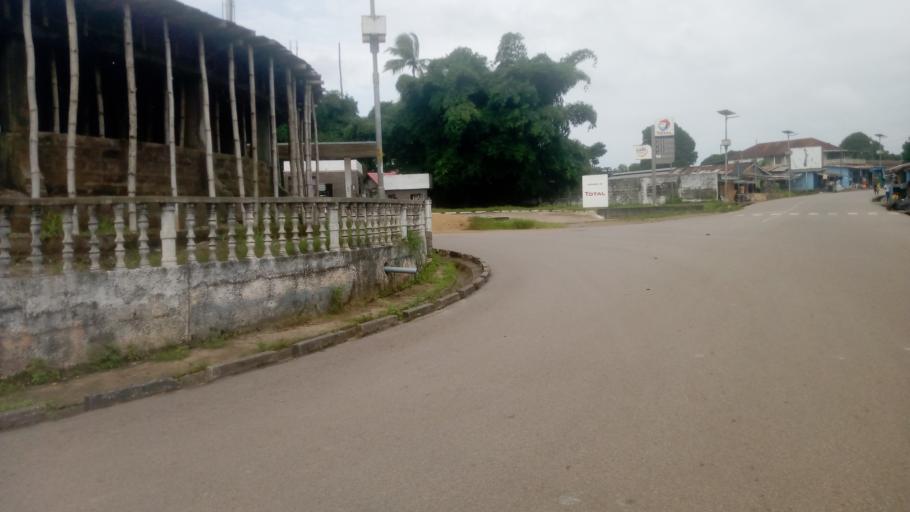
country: SL
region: Northern Province
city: Lunsar
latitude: 8.6858
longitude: -12.5343
